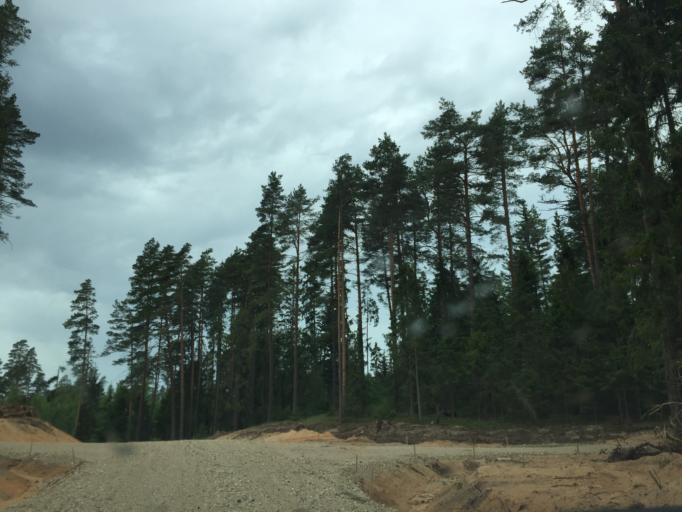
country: LV
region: Tukuma Rajons
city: Tukums
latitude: 57.0340
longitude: 23.0775
